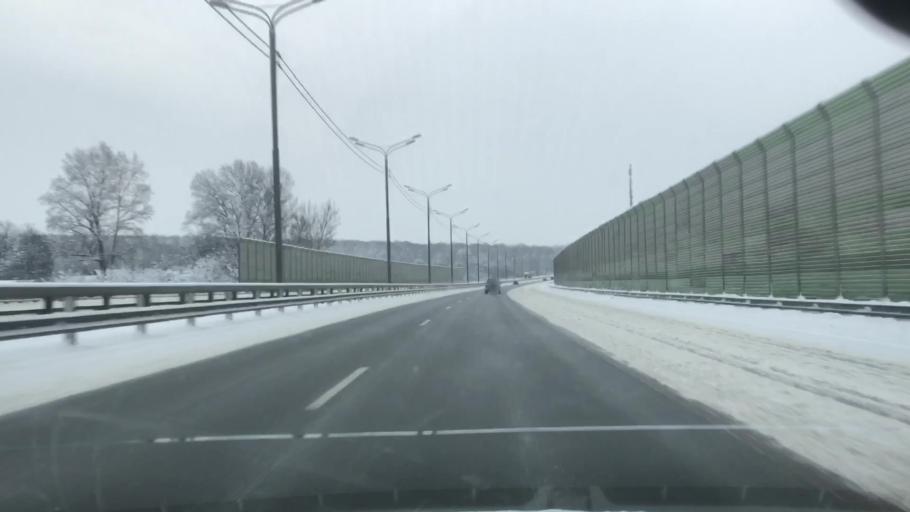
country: RU
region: Moskovskaya
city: Barybino
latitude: 55.2802
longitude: 37.8630
